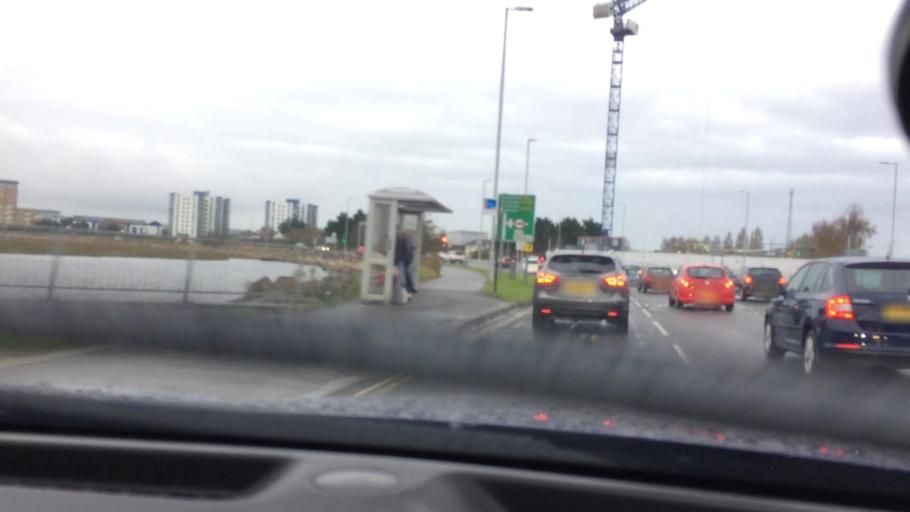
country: GB
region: England
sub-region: Poole
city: Poole
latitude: 50.7192
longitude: -1.9842
